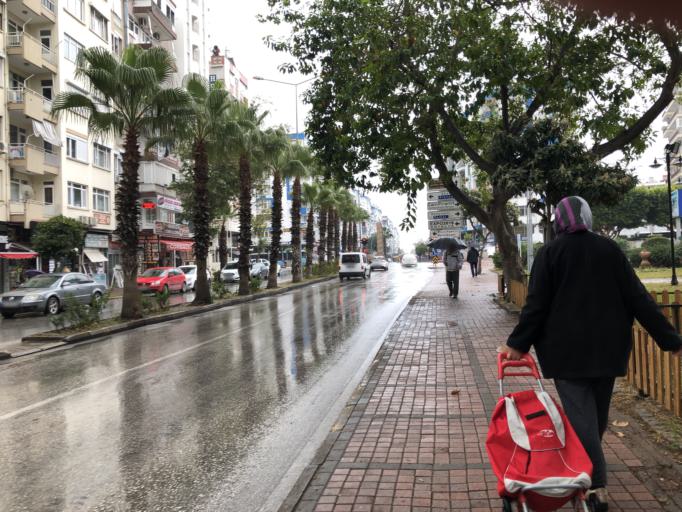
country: TR
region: Antalya
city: Antalya
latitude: 36.8916
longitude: 30.6943
